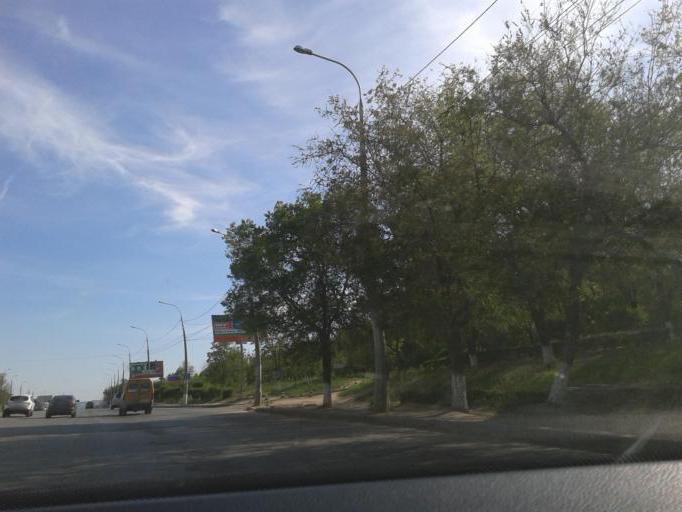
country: RU
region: Volgograd
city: Volgograd
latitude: 48.6741
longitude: 44.4435
